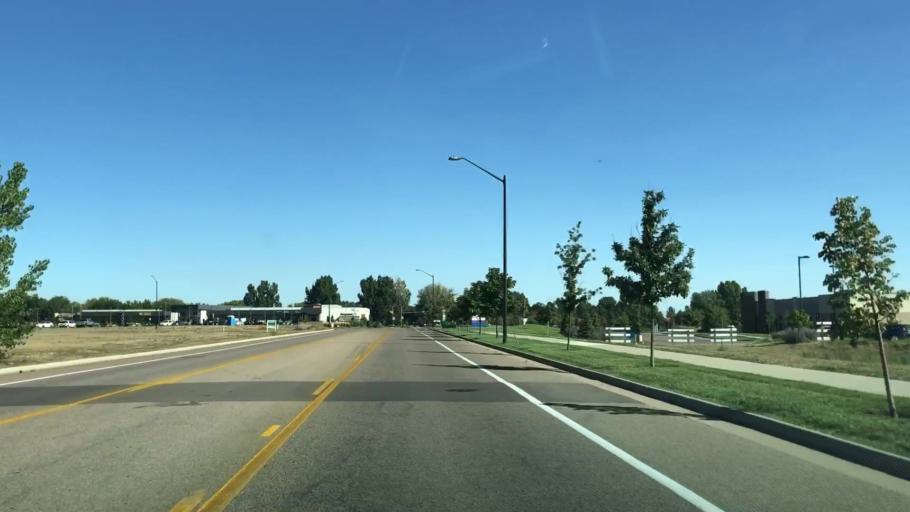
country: US
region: Colorado
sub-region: Larimer County
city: Fort Collins
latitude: 40.5200
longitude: -105.0109
